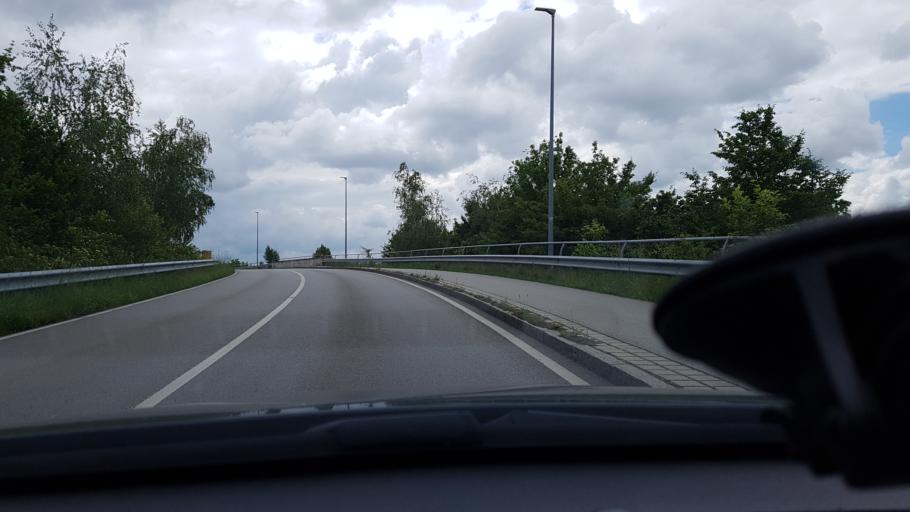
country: DE
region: Bavaria
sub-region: Lower Bavaria
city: Pocking
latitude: 48.4108
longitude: 13.3336
